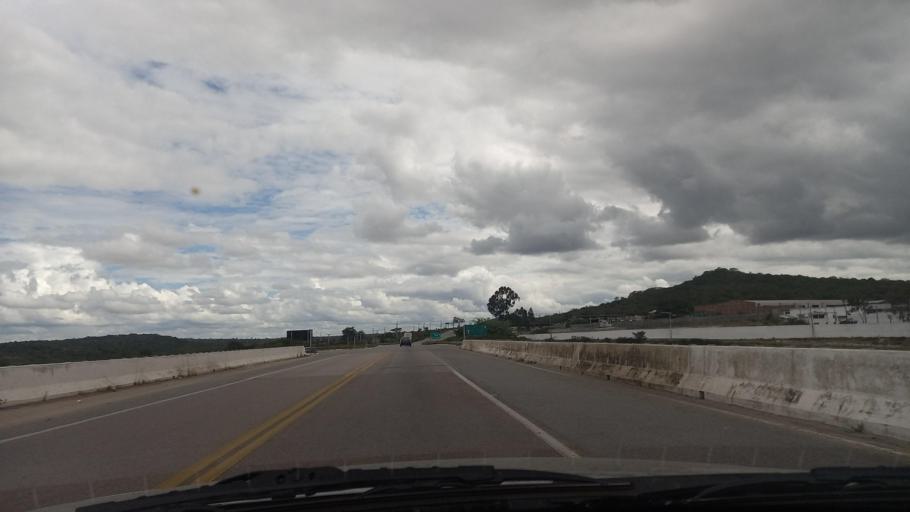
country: BR
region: Pernambuco
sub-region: Caruaru
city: Caruaru
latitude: -8.3294
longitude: -36.1462
